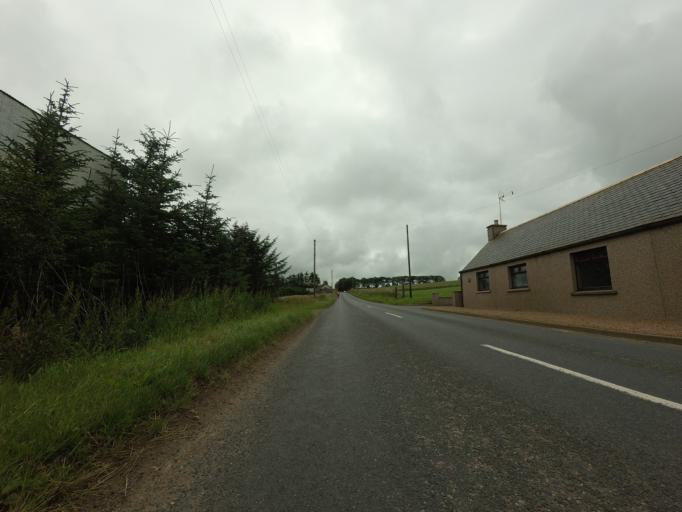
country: GB
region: Scotland
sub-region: Aberdeenshire
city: Turriff
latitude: 57.5424
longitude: -2.3121
